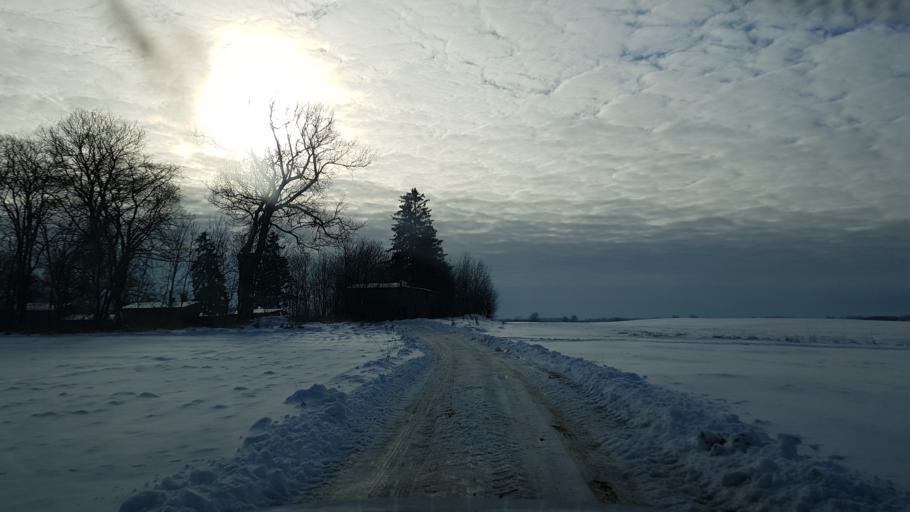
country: PL
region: West Pomeranian Voivodeship
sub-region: Powiat drawski
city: Drawsko Pomorskie
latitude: 53.5368
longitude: 15.7733
